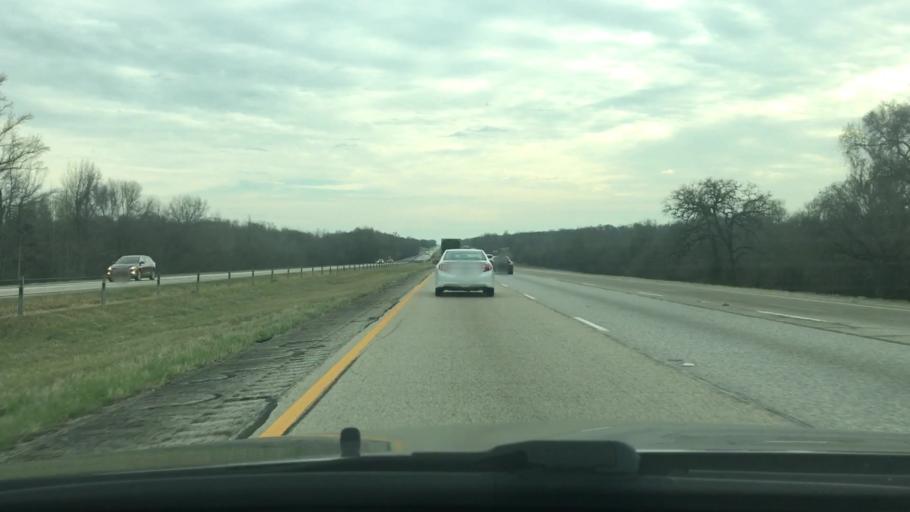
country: US
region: Texas
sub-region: Leon County
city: Centerville
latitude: 31.1922
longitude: -95.9929
